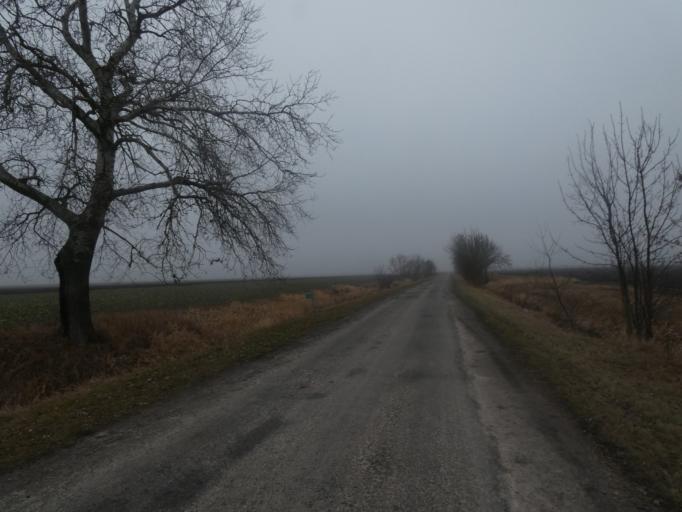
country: HU
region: Pest
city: Tapiogyorgye
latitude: 47.3099
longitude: 19.9738
